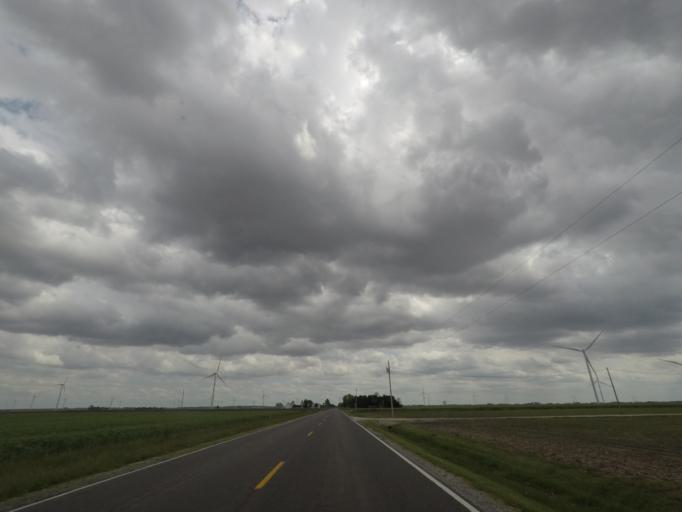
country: US
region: Illinois
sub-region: Macon County
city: Warrensburg
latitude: 40.0072
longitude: -89.0856
